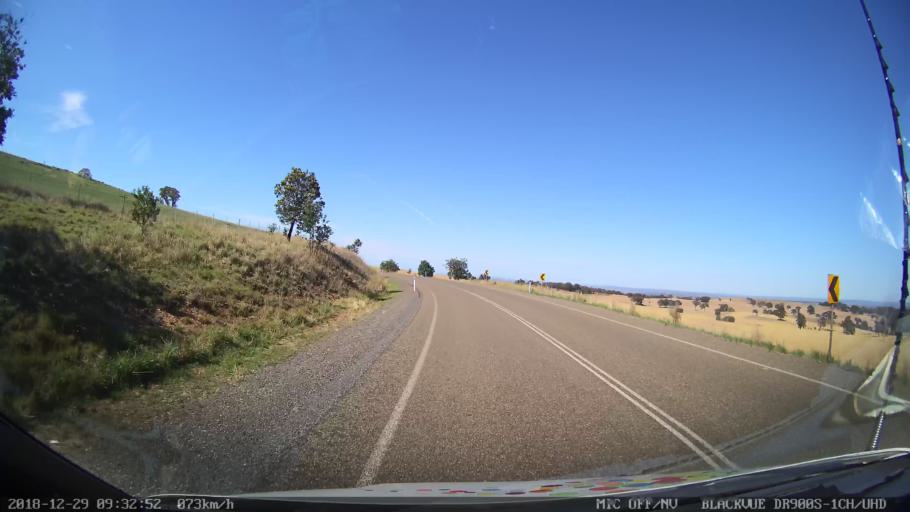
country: AU
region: New South Wales
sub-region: Upper Lachlan Shire
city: Crookwell
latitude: -34.6197
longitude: 149.3500
